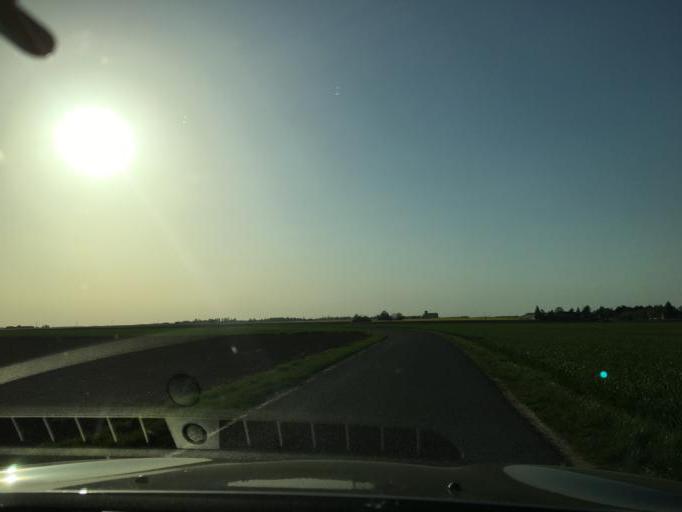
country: FR
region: Centre
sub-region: Departement du Loir-et-Cher
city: Ouzouer-le-Marche
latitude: 47.9018
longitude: 1.5693
